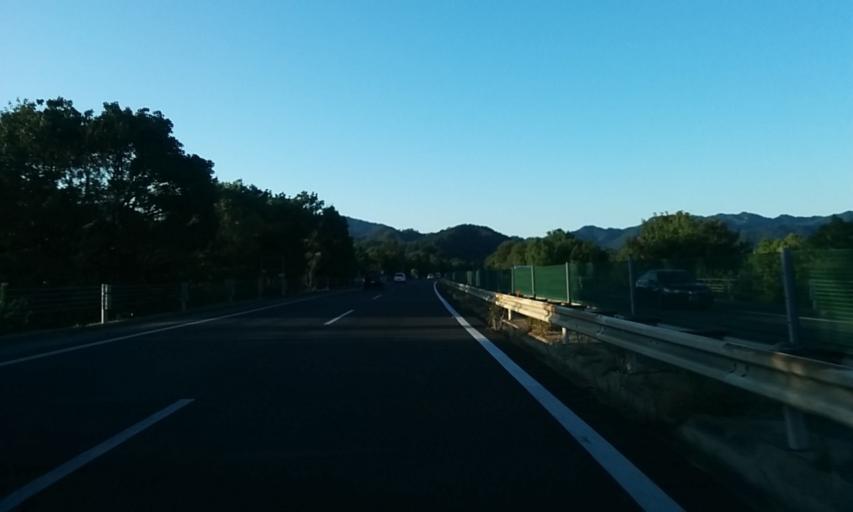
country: JP
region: Hyogo
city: Sasayama
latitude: 35.0816
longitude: 135.1680
